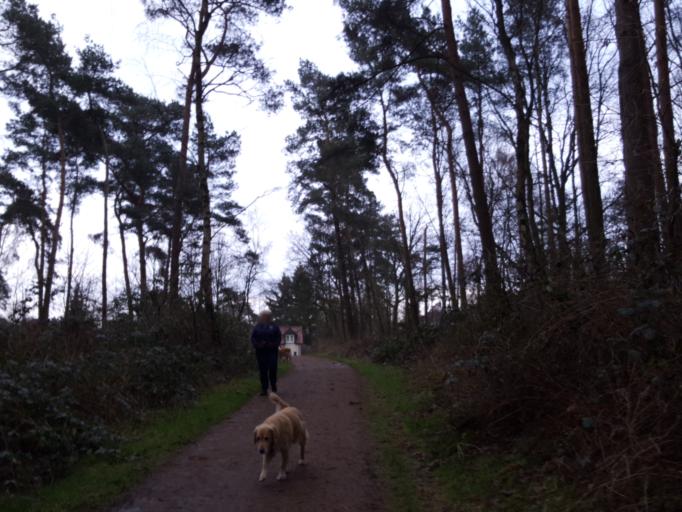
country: DE
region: Hamburg
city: Bergedorf
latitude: 53.4973
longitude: 10.1947
